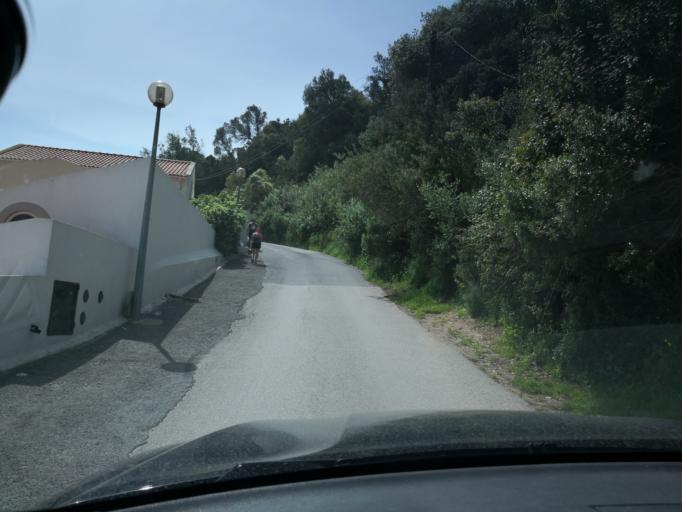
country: PT
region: Setubal
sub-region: Palmela
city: Quinta do Anjo
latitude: 38.4750
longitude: -8.9841
